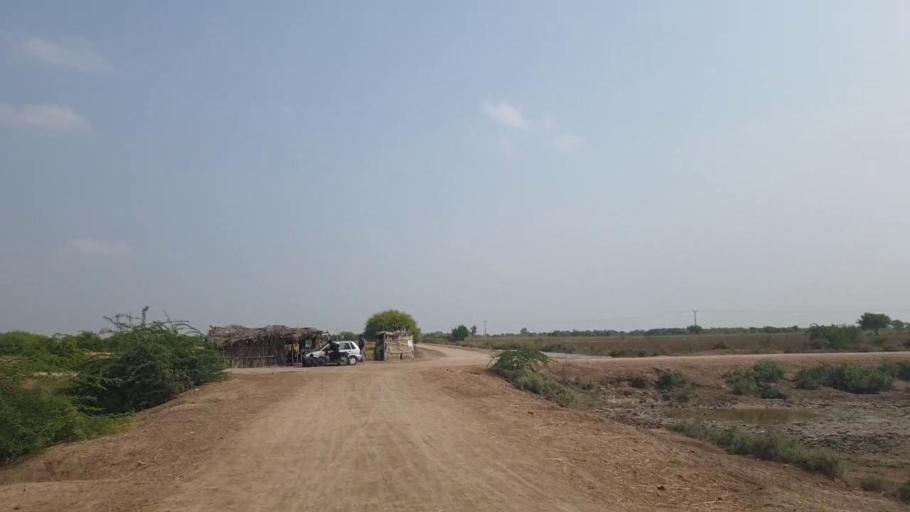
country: PK
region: Sindh
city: Badin
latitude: 24.5475
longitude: 68.7190
